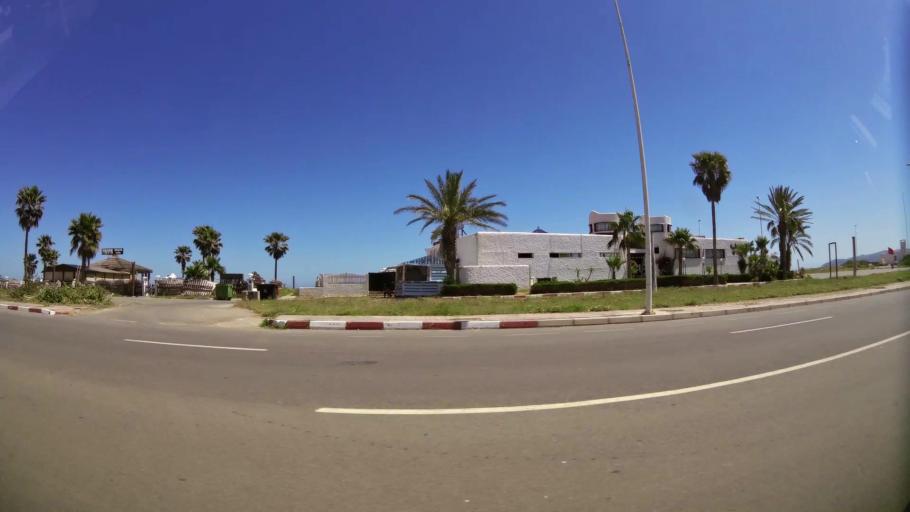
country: MA
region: Oriental
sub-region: Berkane-Taourirt
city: Madagh
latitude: 35.0962
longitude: -2.2622
